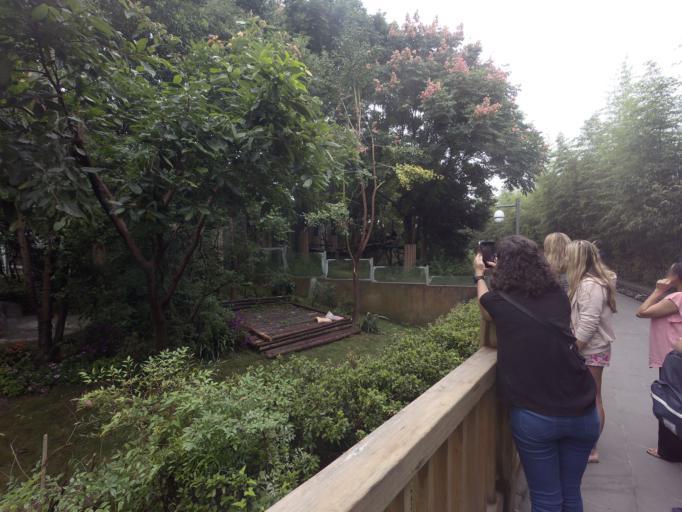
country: CN
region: Sichuan
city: Xindu
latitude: 30.7422
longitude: 104.1375
